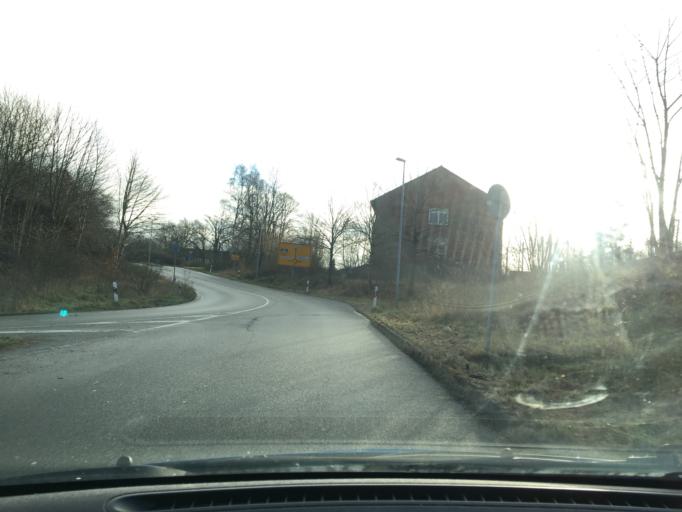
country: DE
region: Lower Saxony
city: Lueneburg
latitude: 53.2521
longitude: 10.4436
